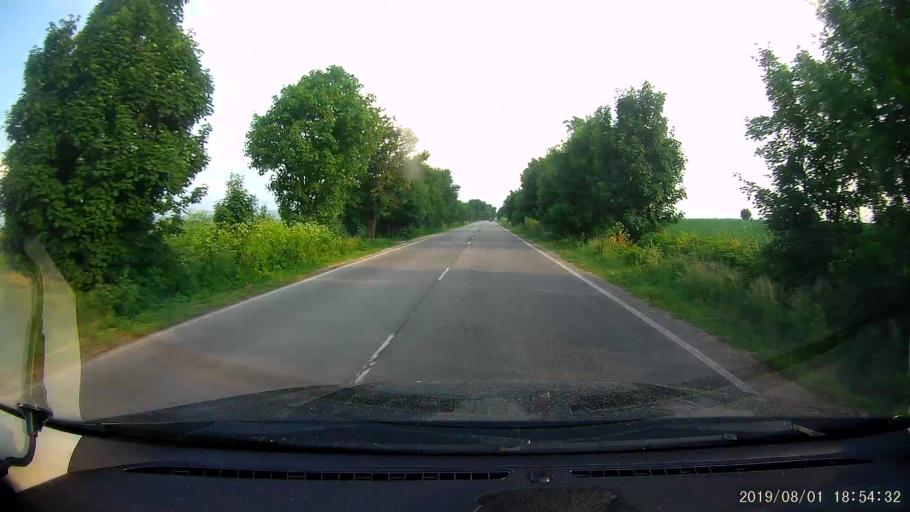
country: BG
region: Shumen
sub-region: Obshtina Shumen
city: Shumen
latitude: 43.1963
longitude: 27.0022
